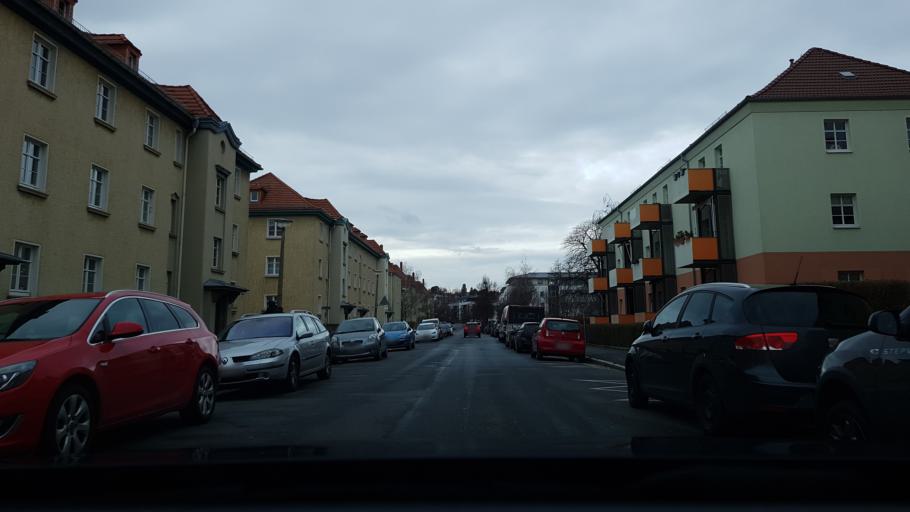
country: DE
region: Saxony
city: Dresden
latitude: 51.0155
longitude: 13.7863
